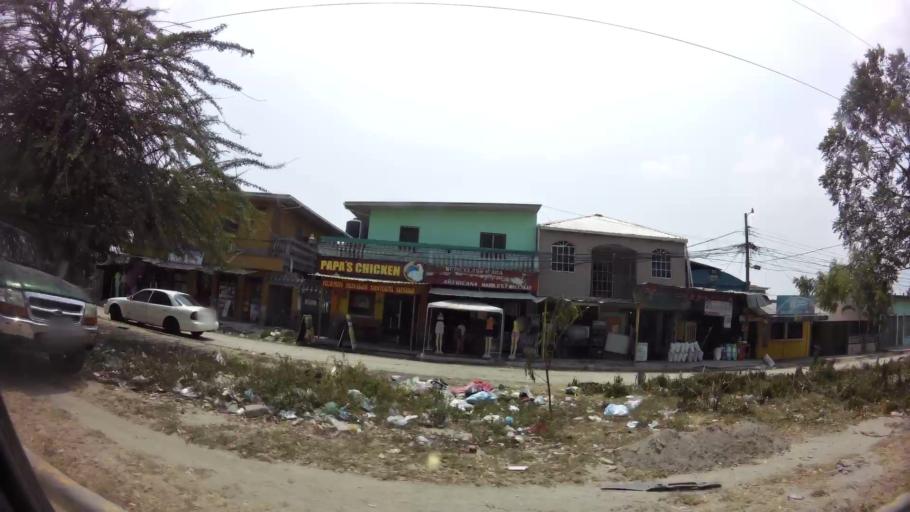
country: HN
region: Cortes
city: San Pedro Sula
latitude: 15.4820
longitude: -87.9831
